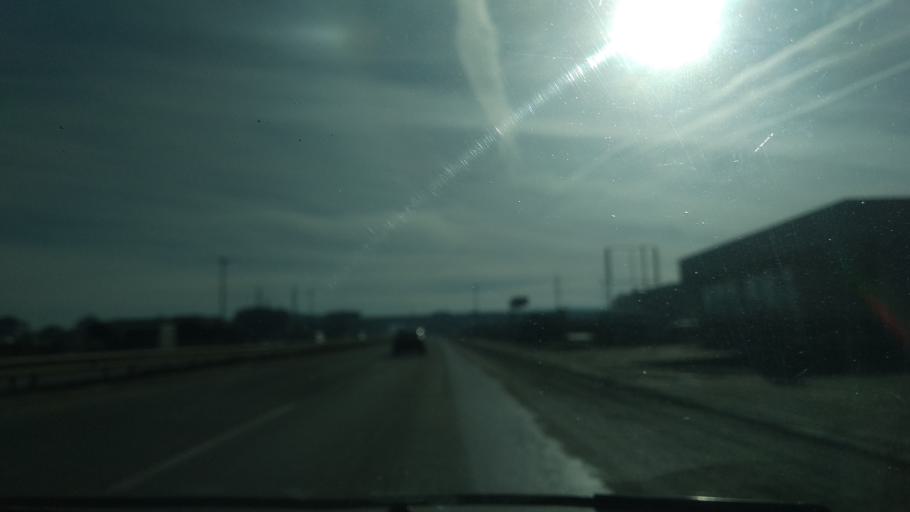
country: XK
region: Pristina
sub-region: Komuna e Obiliqit
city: Obiliq
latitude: 42.7043
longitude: 21.1075
